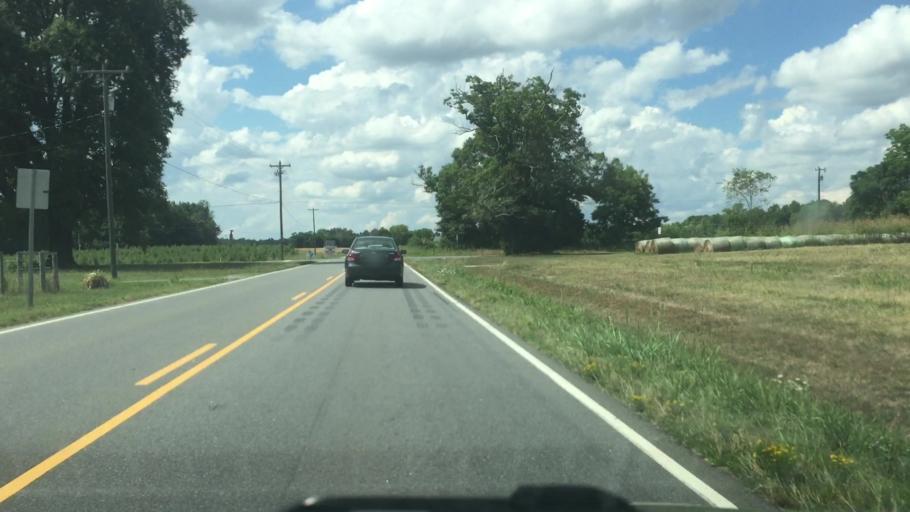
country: US
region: North Carolina
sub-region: Gaston County
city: Davidson
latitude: 35.4852
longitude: -80.7583
